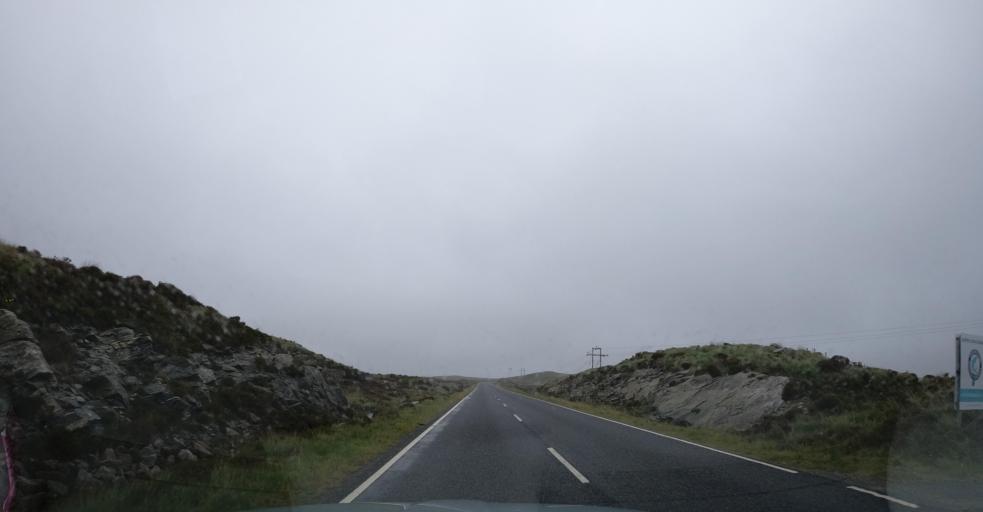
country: GB
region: Scotland
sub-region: Eilean Siar
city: Isle of North Uist
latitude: 57.5847
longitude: -7.2380
